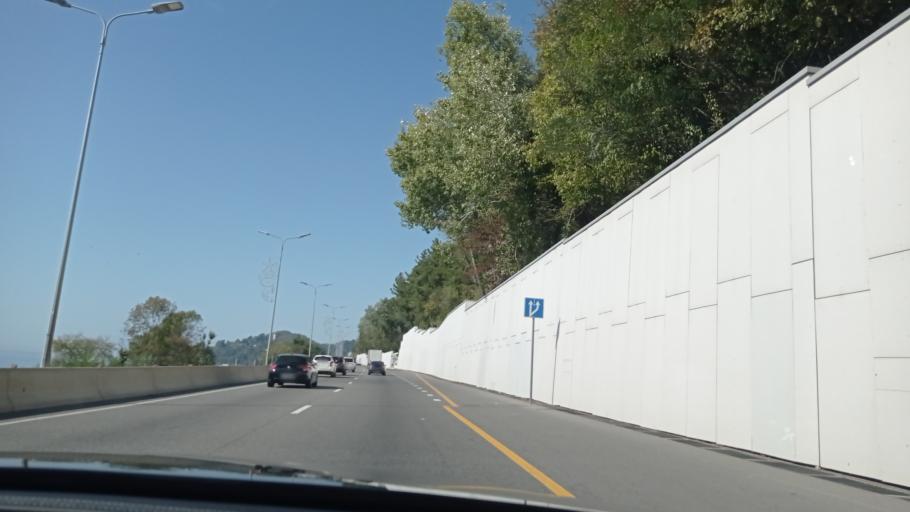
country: RU
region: Krasnodarskiy
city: Kudepsta
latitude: 43.4997
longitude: 39.8794
